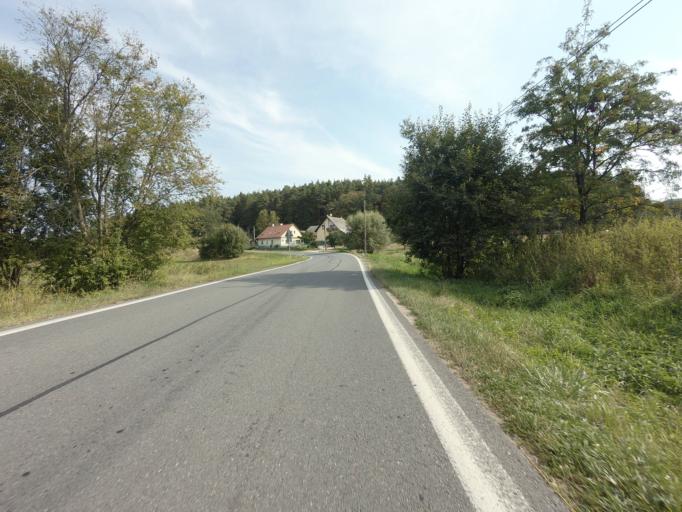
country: CZ
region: Central Bohemia
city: Petrovice
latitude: 49.5381
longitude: 14.3507
